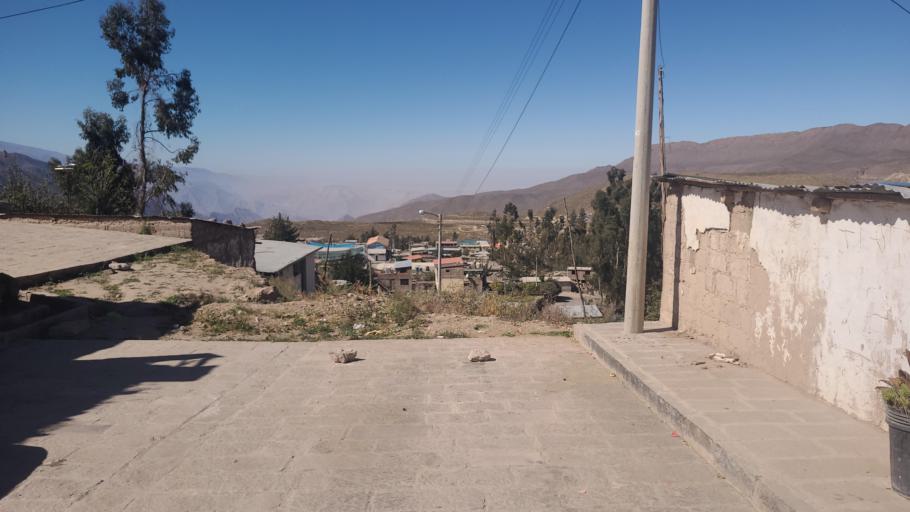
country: PE
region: Arequipa
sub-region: Provincia de Condesuyos
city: Chuquibamba
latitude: -15.8392
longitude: -72.6553
